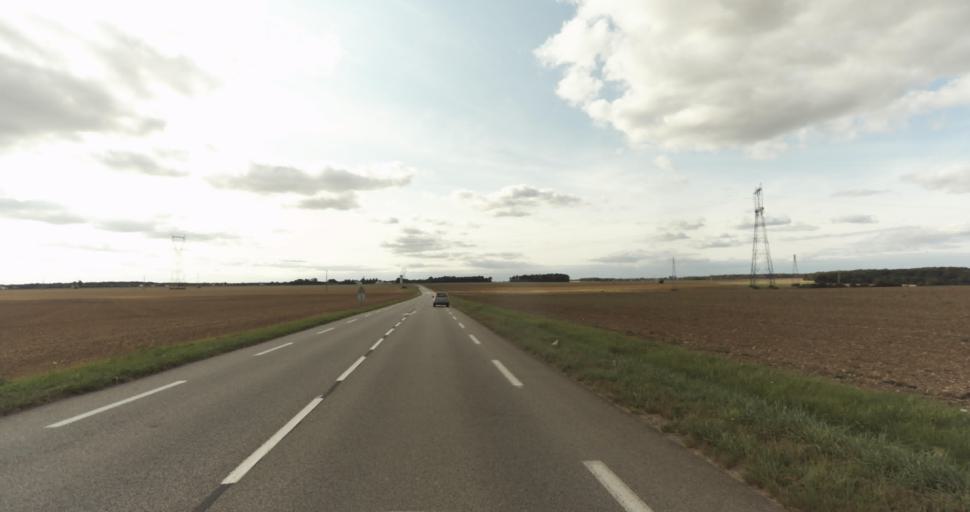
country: FR
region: Haute-Normandie
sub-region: Departement de l'Eure
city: Garennes-sur-Eure
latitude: 48.8924
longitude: 1.4272
